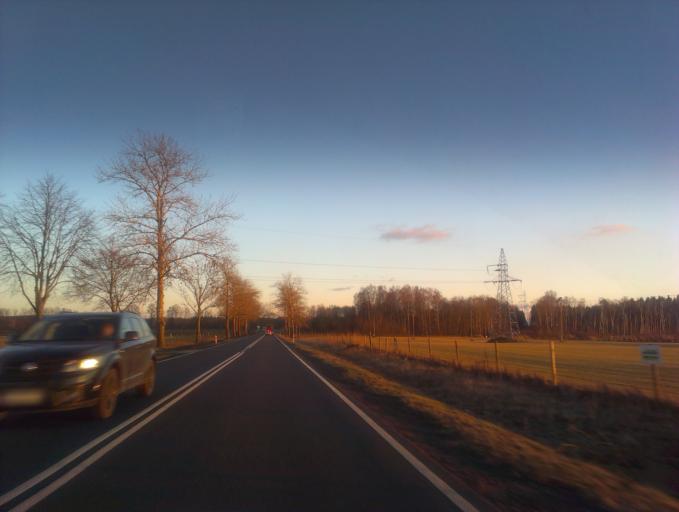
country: PL
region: West Pomeranian Voivodeship
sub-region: Powiat szczecinecki
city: Szczecinek
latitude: 53.6458
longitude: 16.7541
